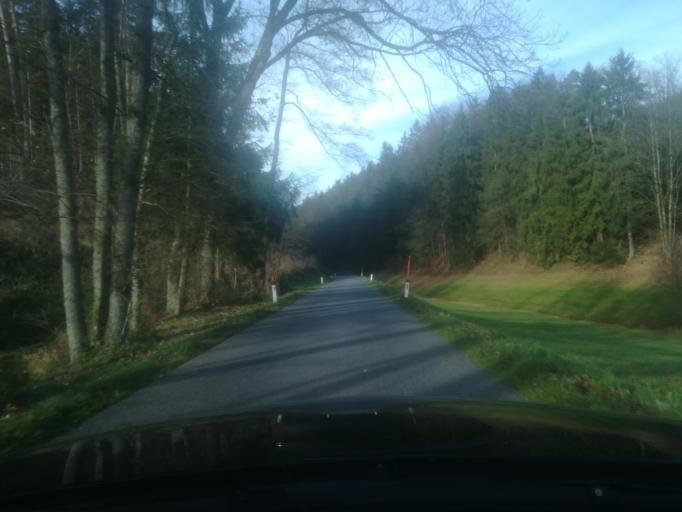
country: AT
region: Upper Austria
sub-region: Politischer Bezirk Perg
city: Perg
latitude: 48.3343
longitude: 14.6482
